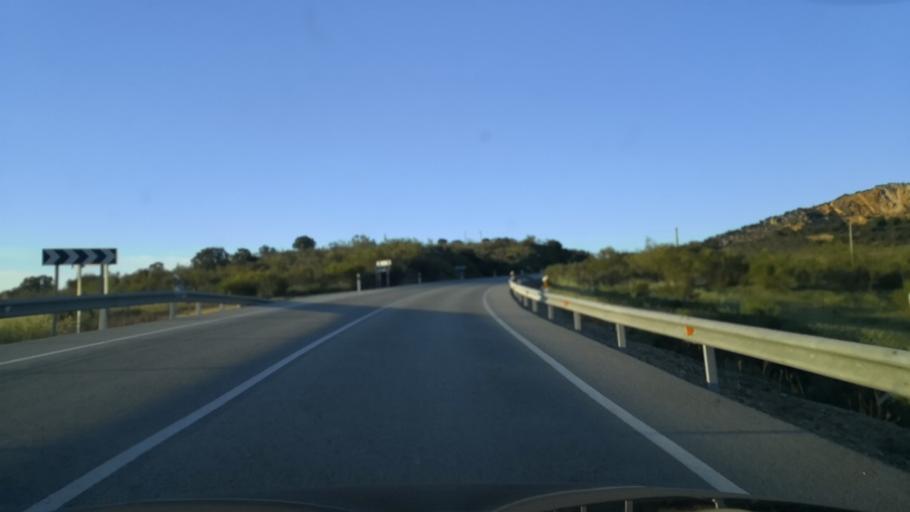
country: ES
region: Extremadura
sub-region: Provincia de Caceres
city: Valencia de Alcantara
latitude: 39.4780
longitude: -7.2120
